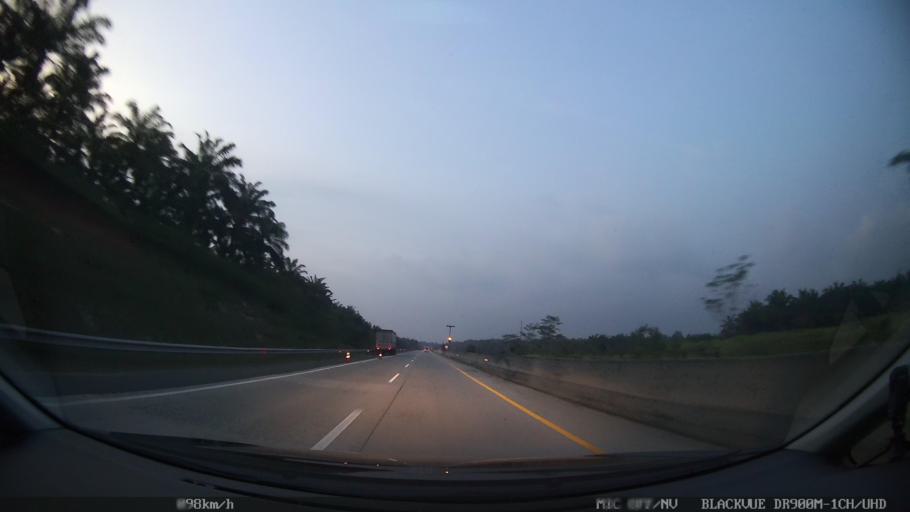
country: ID
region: Lampung
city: Sidorejo
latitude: -5.5500
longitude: 105.5245
